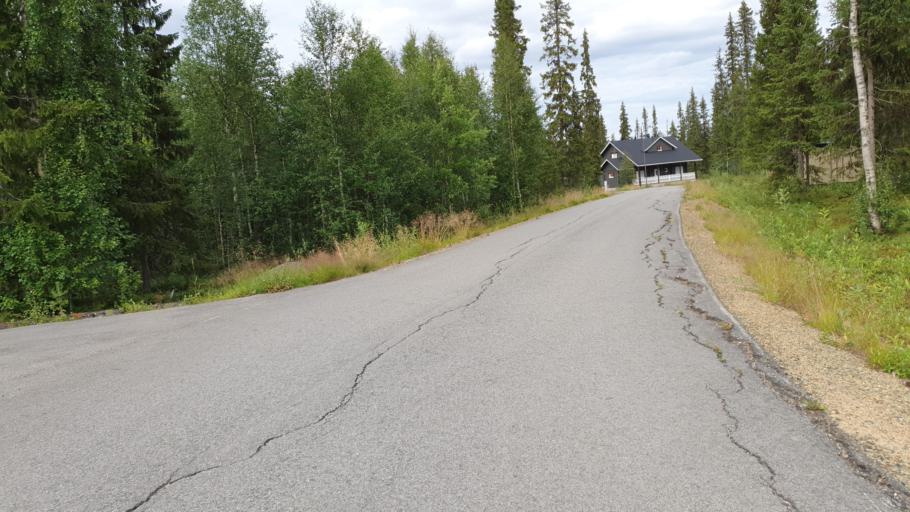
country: FI
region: Lapland
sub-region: Tunturi-Lappi
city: Kolari
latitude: 67.6013
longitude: 24.1425
